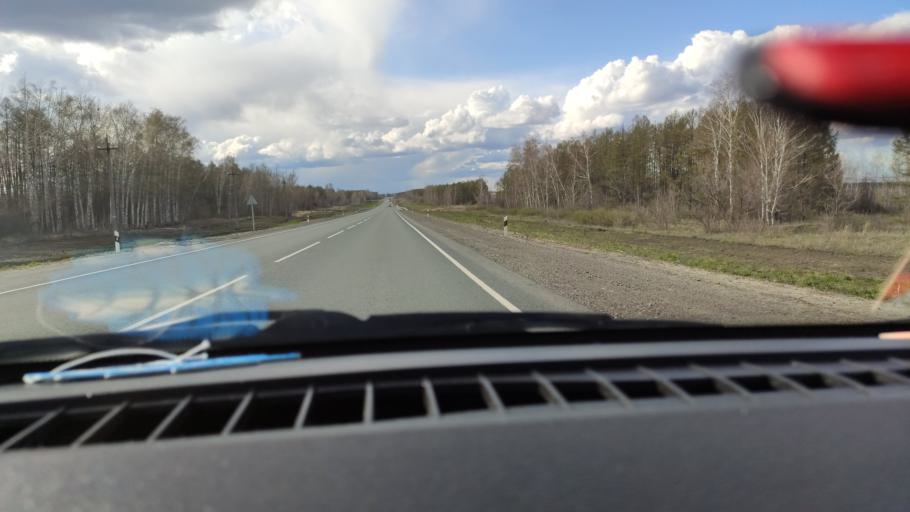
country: RU
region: Saratov
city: Shikhany
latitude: 52.1541
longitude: 47.1816
